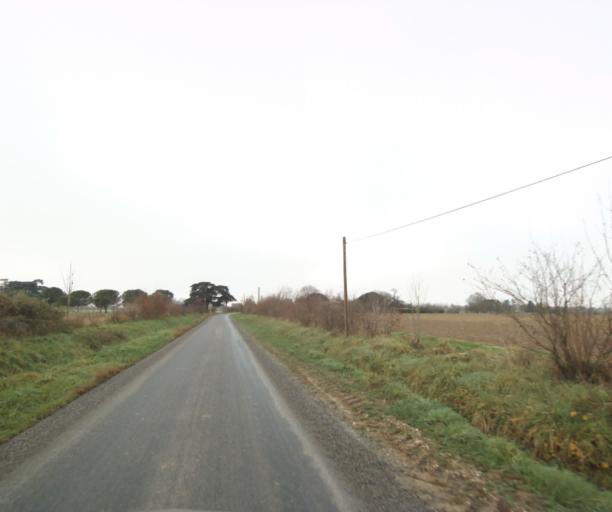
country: FR
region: Midi-Pyrenees
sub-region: Departement de la Haute-Garonne
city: Villemur-sur-Tarn
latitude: 43.8698
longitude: 1.4866
